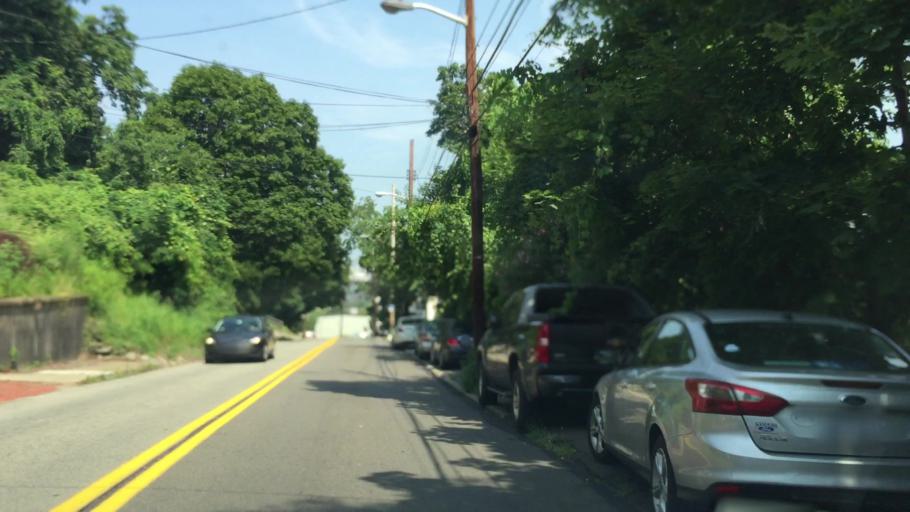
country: US
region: Pennsylvania
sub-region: Allegheny County
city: Mount Oliver
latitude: 40.4215
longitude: -79.9644
